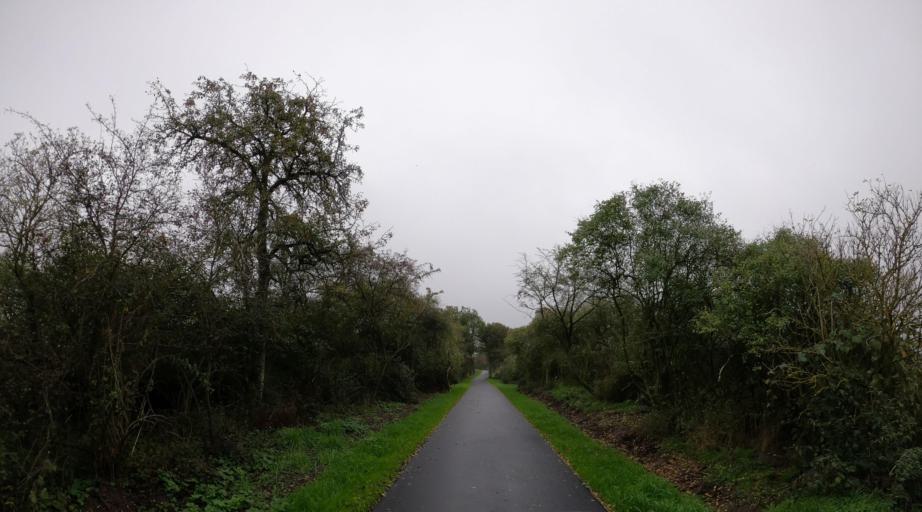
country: PL
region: West Pomeranian Voivodeship
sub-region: Powiat mysliborski
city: Mysliborz
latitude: 52.9128
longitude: 14.7457
